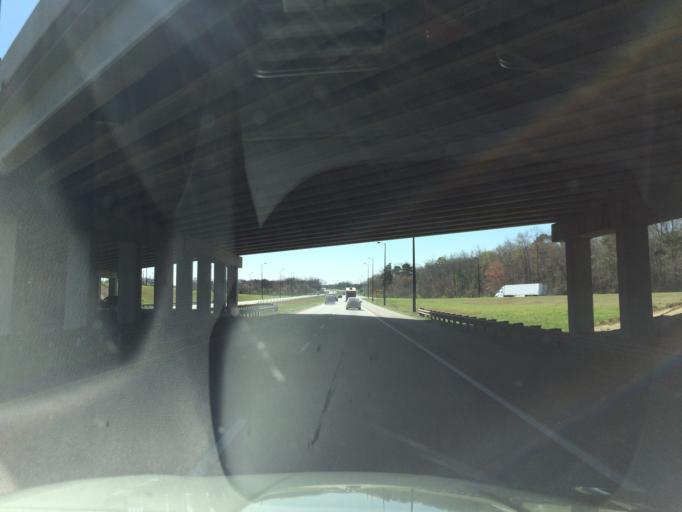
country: US
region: Alabama
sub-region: Lee County
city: Auburn
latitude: 32.5595
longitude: -85.5051
